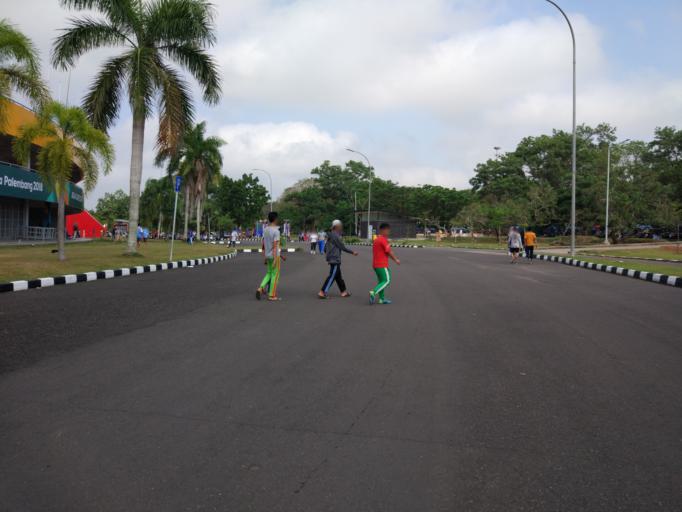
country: ID
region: South Sumatra
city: Plaju
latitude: -3.0204
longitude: 104.7897
